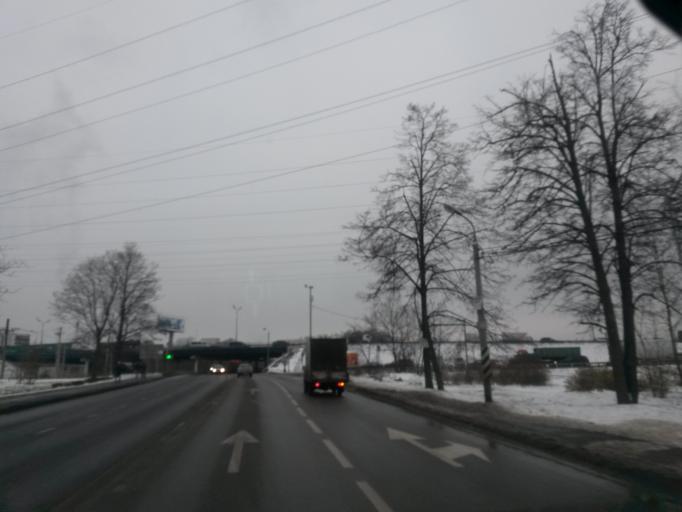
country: RU
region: Moscow
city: Mikhalkovo
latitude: 55.6691
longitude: 37.4297
